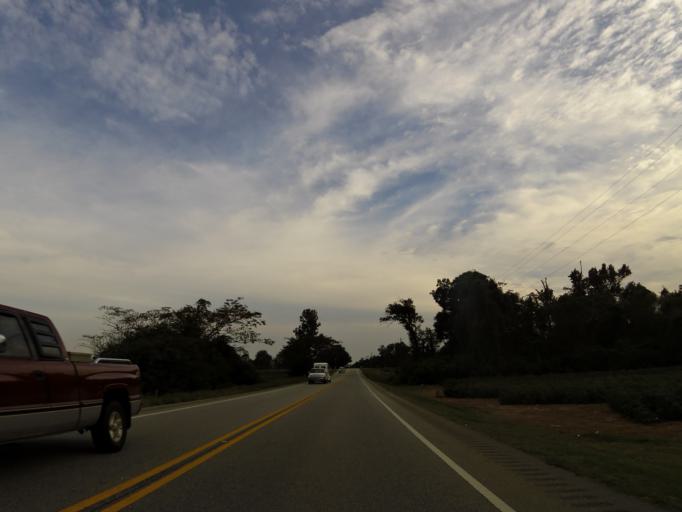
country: US
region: Alabama
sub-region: Monroe County
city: Frisco City
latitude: 31.2778
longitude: -87.5025
